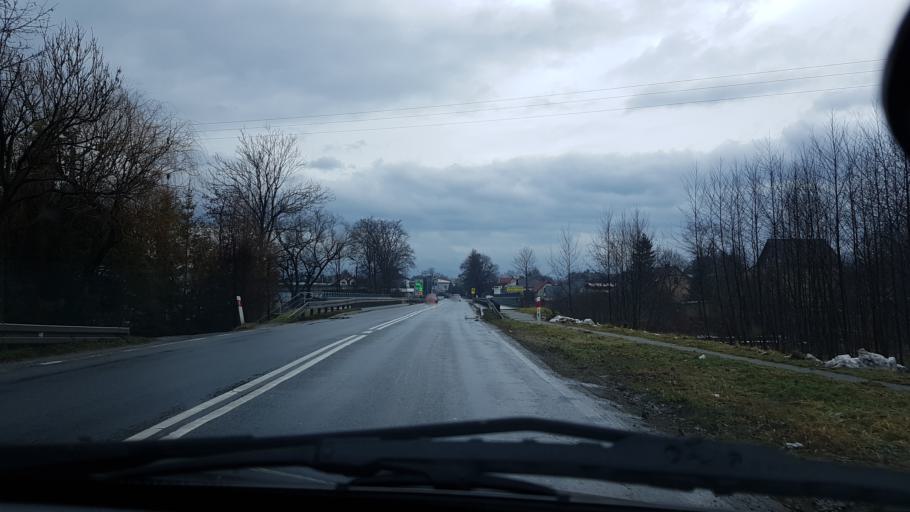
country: PL
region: Silesian Voivodeship
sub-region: Powiat zywiecki
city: Lodygowice
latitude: 49.7279
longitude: 19.1353
